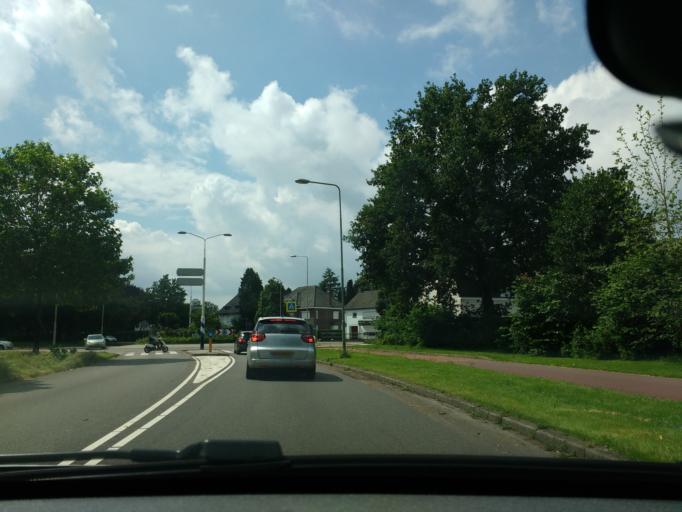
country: NL
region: Limburg
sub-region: Gemeente Venray
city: Venray
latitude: 51.5295
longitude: 5.9834
